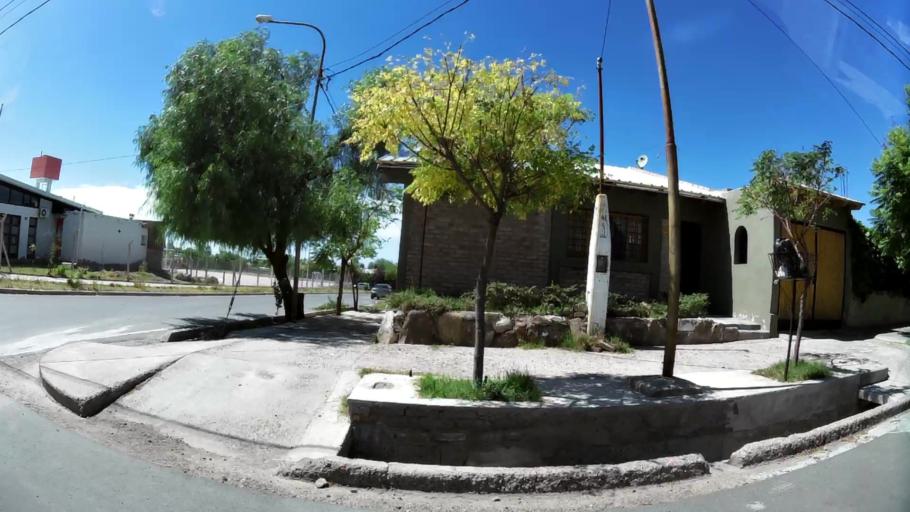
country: AR
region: Mendoza
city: Las Heras
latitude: -32.8468
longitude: -68.8745
